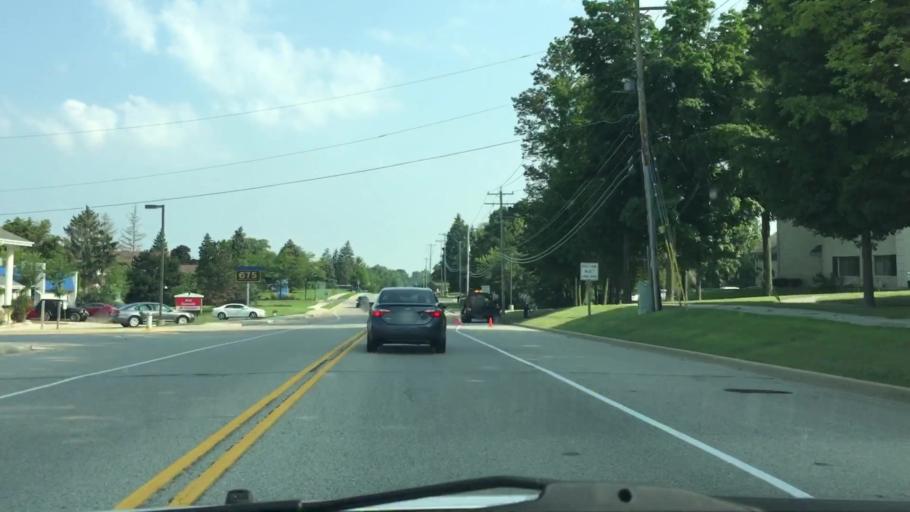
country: US
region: Wisconsin
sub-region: Waukesha County
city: Brookfield
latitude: 43.0381
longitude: -88.1467
